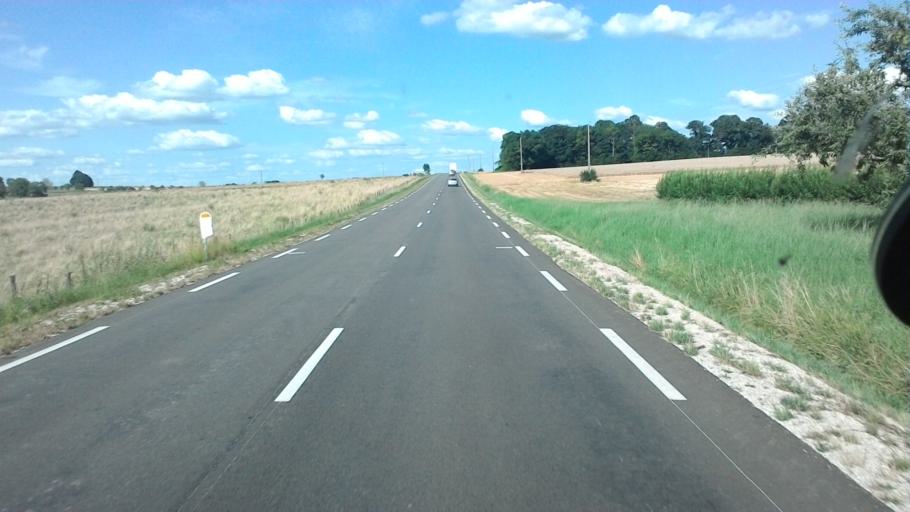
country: FR
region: Franche-Comte
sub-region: Departement de la Haute-Saone
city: Gy
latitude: 47.4579
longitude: 5.9045
